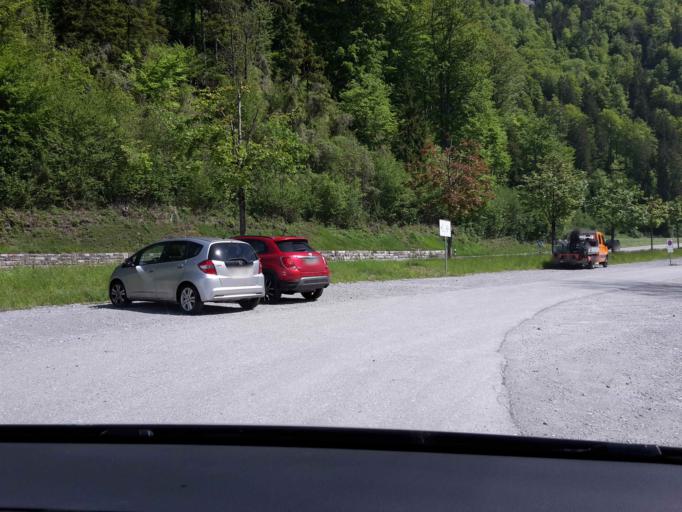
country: CH
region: Bern
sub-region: Frutigen-Niedersimmental District
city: Wimmis
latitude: 46.6693
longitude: 7.6063
